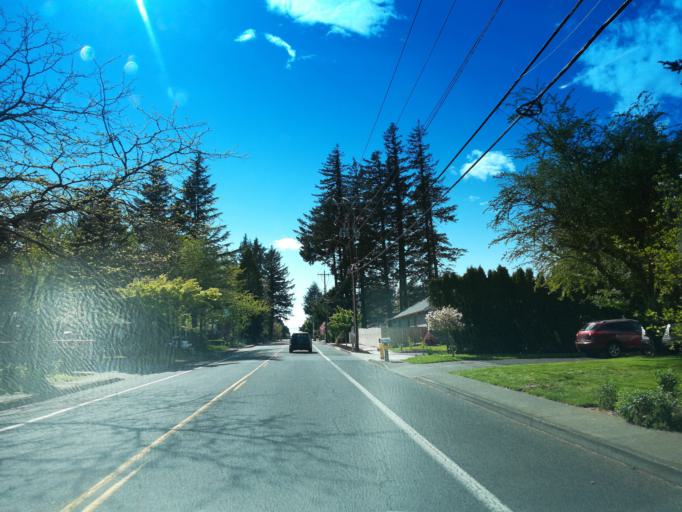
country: US
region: Oregon
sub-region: Multnomah County
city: Troutdale
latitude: 45.5336
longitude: -122.3893
